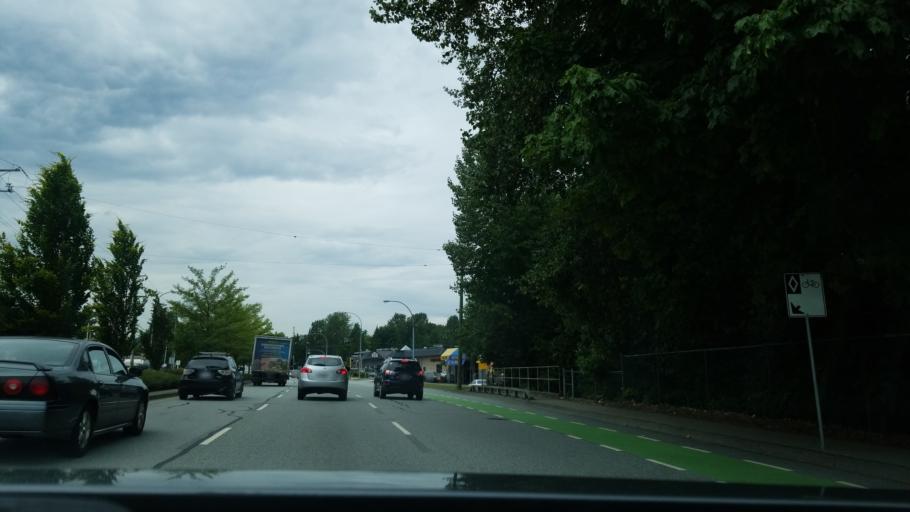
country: CA
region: British Columbia
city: Port Moody
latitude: 49.2777
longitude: -122.8043
